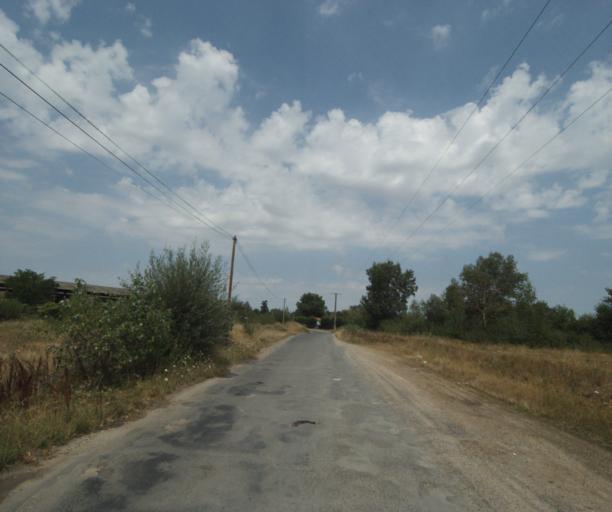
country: FR
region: Bourgogne
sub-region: Departement de Saone-et-Loire
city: Gueugnon
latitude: 46.5867
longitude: 4.0551
